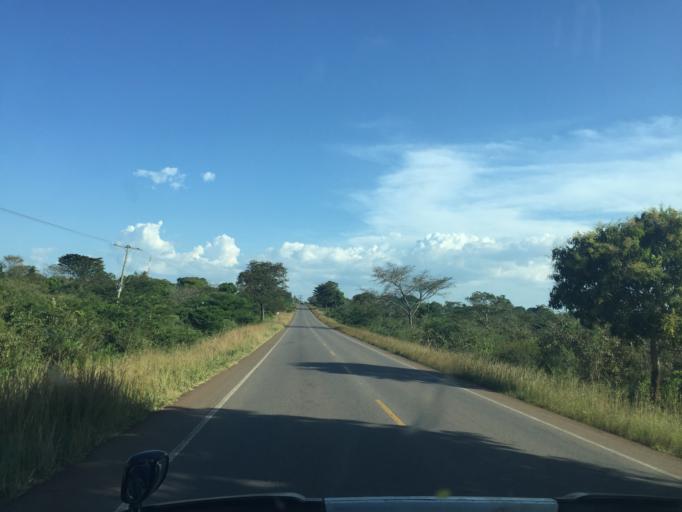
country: UG
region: Central Region
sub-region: Nakasongola District
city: Nakasongola
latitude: 1.2563
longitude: 32.4546
